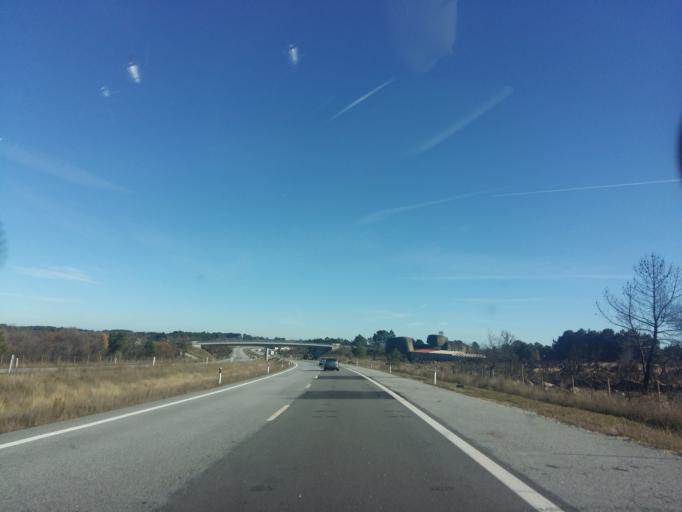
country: PT
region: Guarda
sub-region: Guarda
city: Sequeira
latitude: 40.6006
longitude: -7.1146
